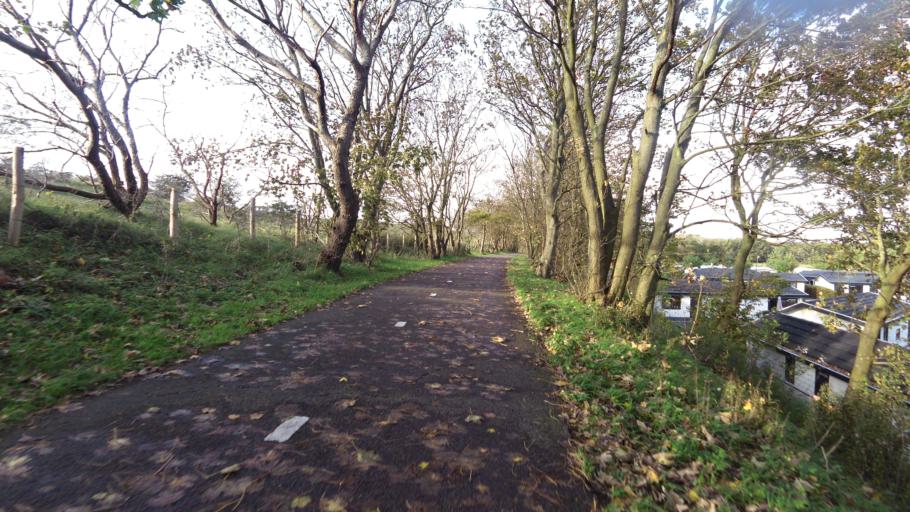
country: NL
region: South Holland
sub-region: Gemeente Noordwijkerhout
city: Noordwijkerhout
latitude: 52.2879
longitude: 4.4871
